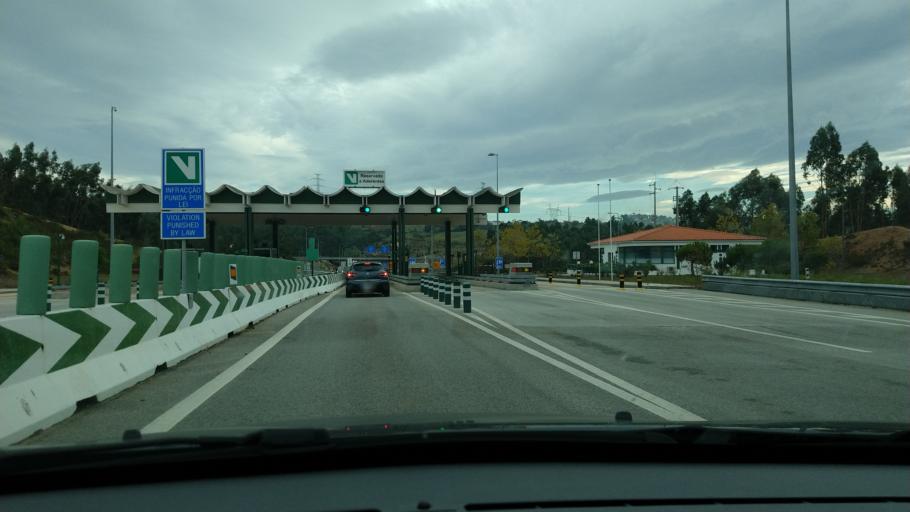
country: PT
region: Coimbra
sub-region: Figueira da Foz
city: Alhadas
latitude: 40.1560
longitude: -8.7798
